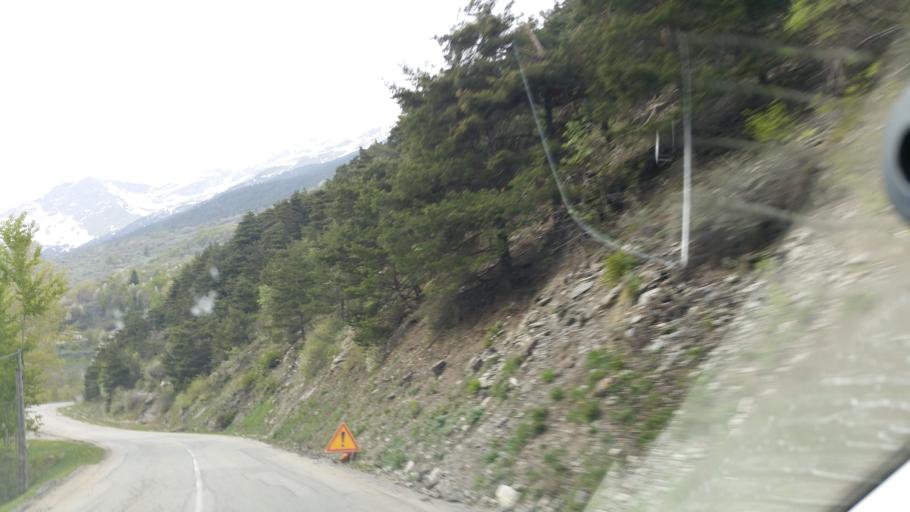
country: FR
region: Rhone-Alpes
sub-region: Departement de la Savoie
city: Modane
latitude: 45.1962
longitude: 6.6294
